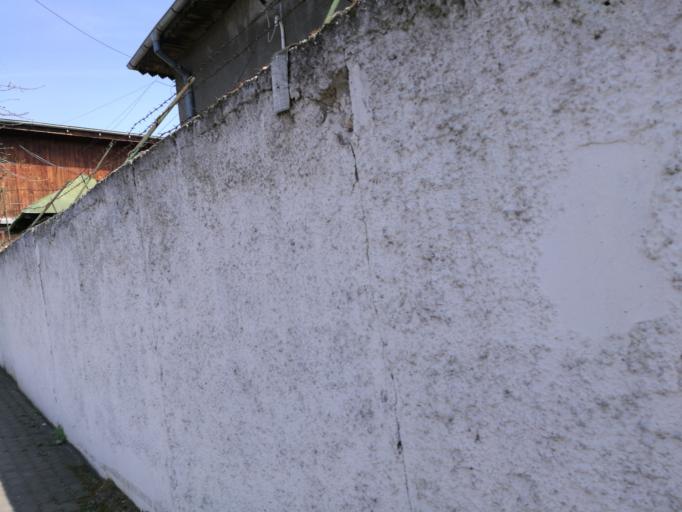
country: RO
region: Ilfov
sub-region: Comuna Chiajna
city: Rosu
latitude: 44.4779
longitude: 26.0266
